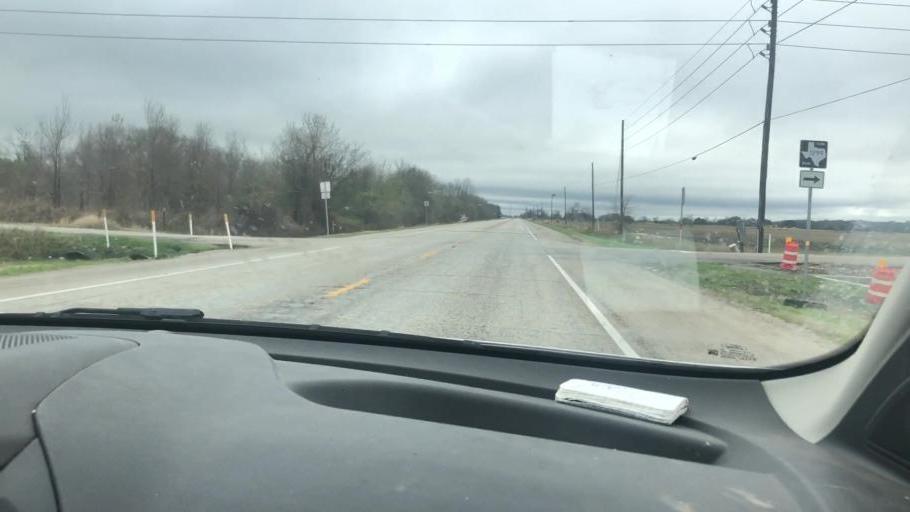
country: US
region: Texas
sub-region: Wharton County
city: Wharton
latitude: 29.2630
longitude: -96.0556
